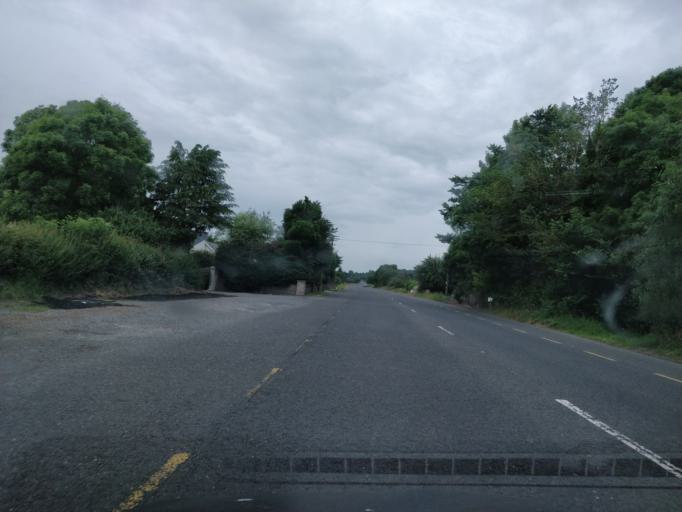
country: IE
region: Munster
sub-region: North Tipperary
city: Roscrea
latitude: 52.9534
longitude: -7.6958
